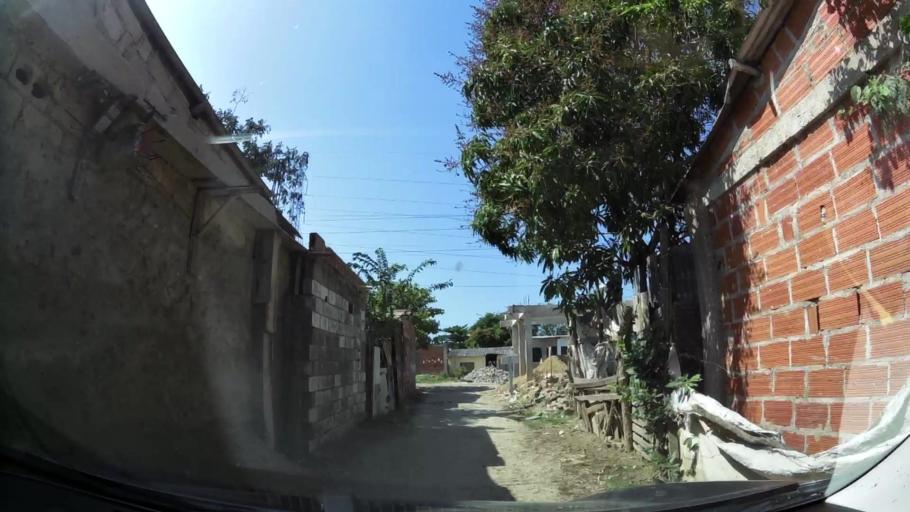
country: CO
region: Bolivar
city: Cartagena
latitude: 10.3728
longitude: -75.4677
